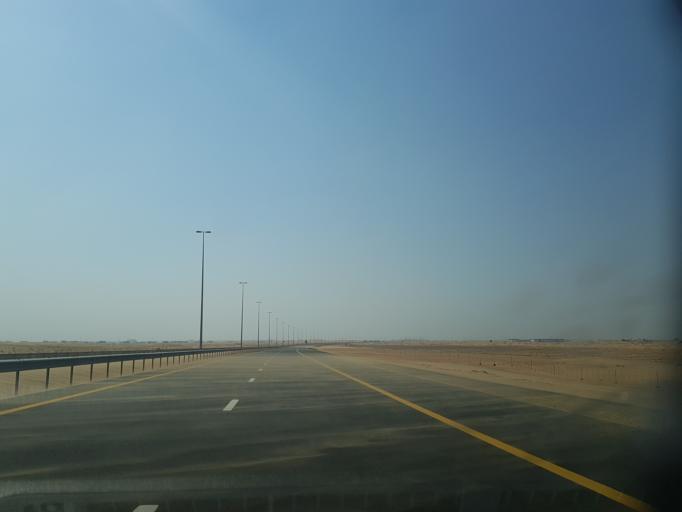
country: AE
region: Ash Shariqah
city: Sharjah
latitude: 25.2715
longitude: 55.6379
